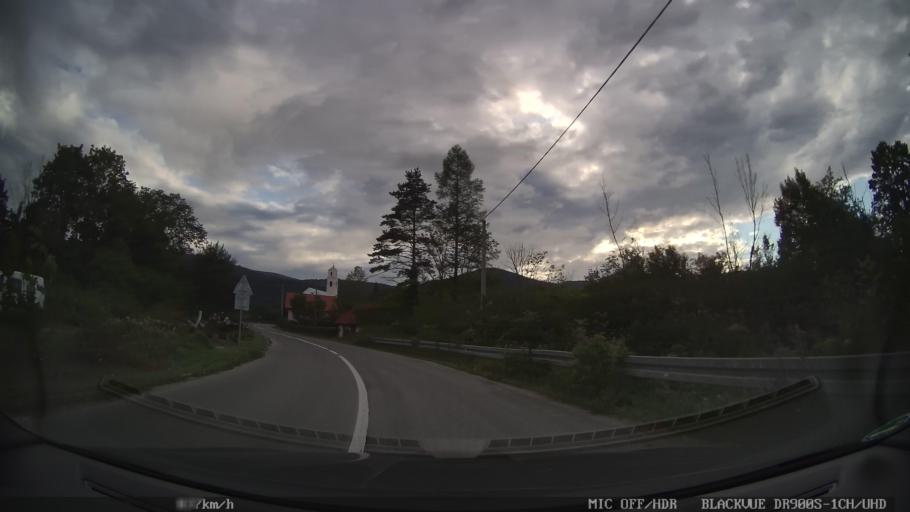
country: HR
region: Karlovacka
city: Plaski
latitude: 44.9969
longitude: 15.4417
